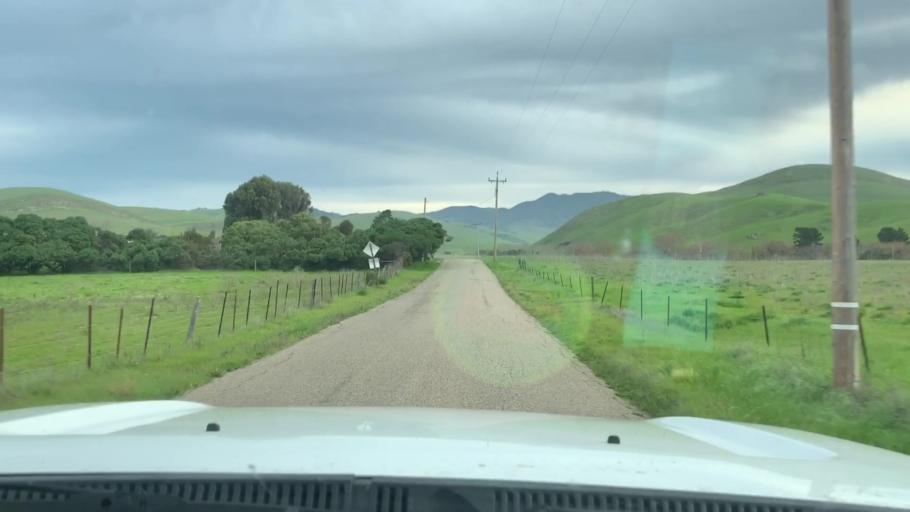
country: US
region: California
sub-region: San Luis Obispo County
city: Morro Bay
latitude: 35.3656
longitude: -120.8057
